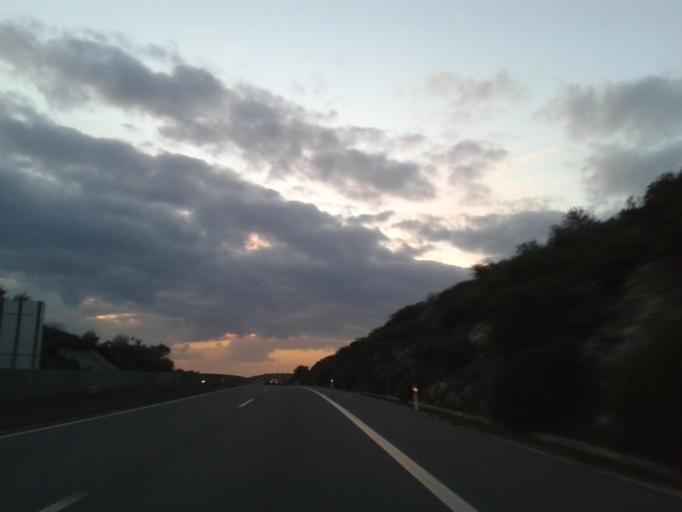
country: PT
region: Faro
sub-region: Loule
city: Boliqueime
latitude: 37.1503
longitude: -8.1501
